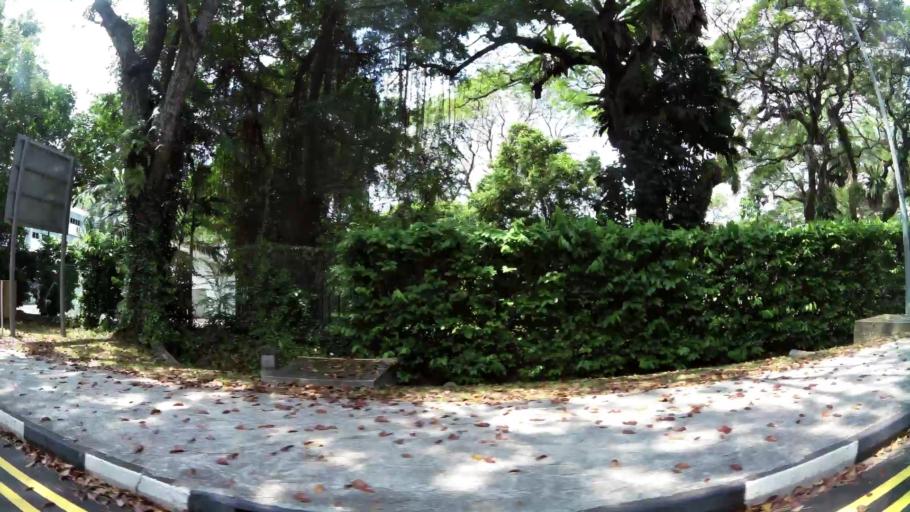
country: SG
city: Singapore
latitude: 1.2895
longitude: 103.8258
